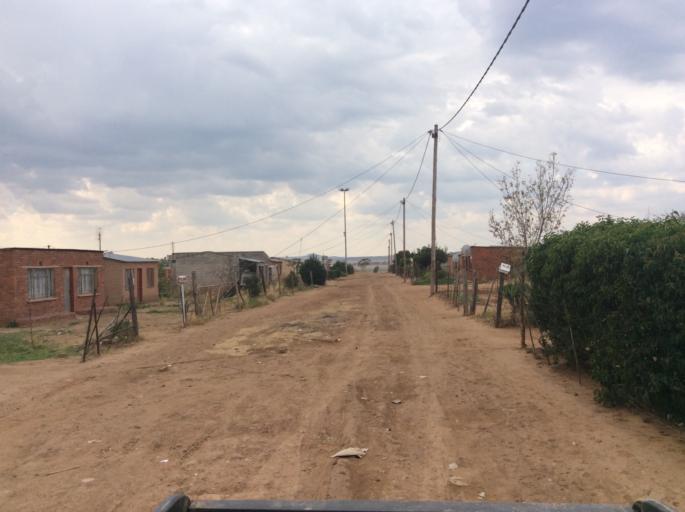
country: ZA
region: Orange Free State
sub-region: Xhariep District Municipality
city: Dewetsdorp
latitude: -29.5760
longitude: 26.6834
